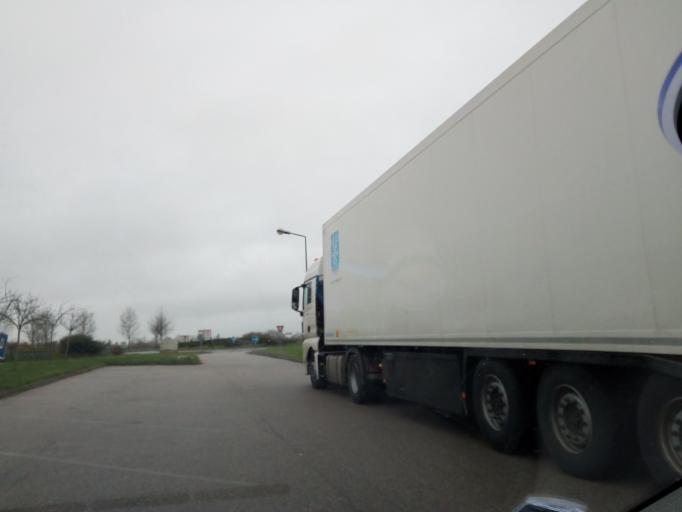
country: FR
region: Lower Normandy
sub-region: Departement de l'Orne
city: Gace
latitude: 48.8499
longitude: 0.3741
